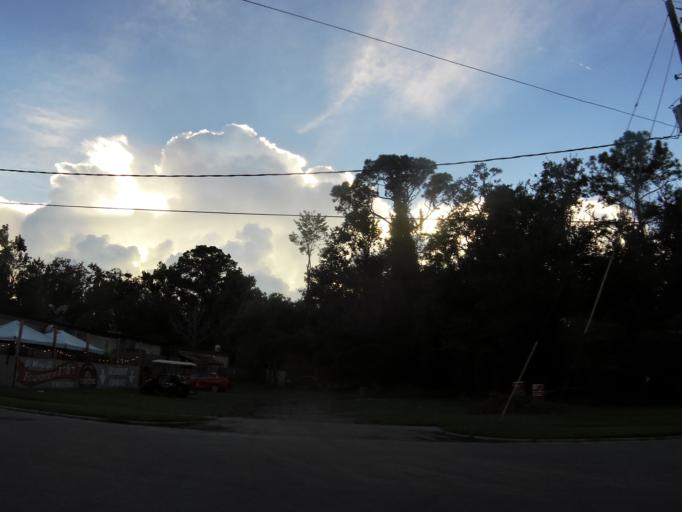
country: US
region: Georgia
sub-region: Camden County
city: St. Marys
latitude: 30.7298
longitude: -81.5464
